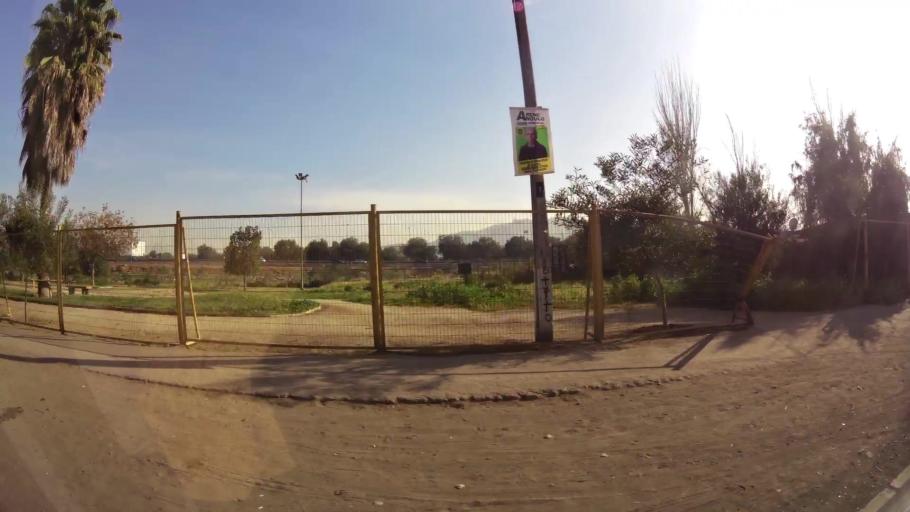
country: CL
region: Santiago Metropolitan
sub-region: Provincia de Santiago
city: Lo Prado
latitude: -33.4130
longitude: -70.7432
